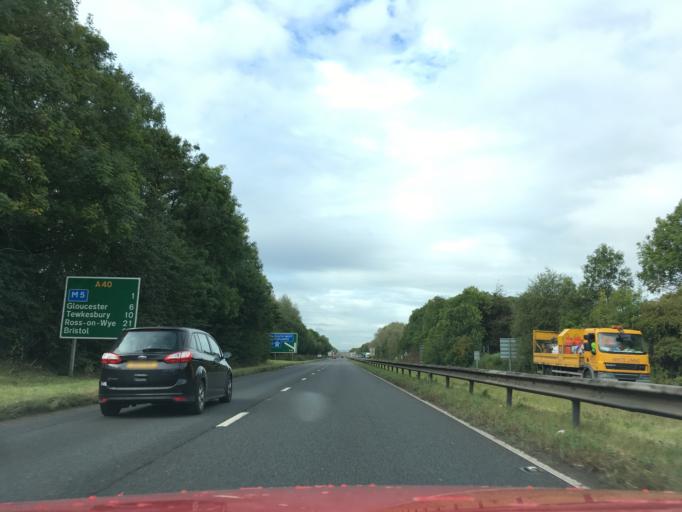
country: GB
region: England
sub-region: Gloucestershire
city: Uckington
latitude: 51.8939
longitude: -2.1319
